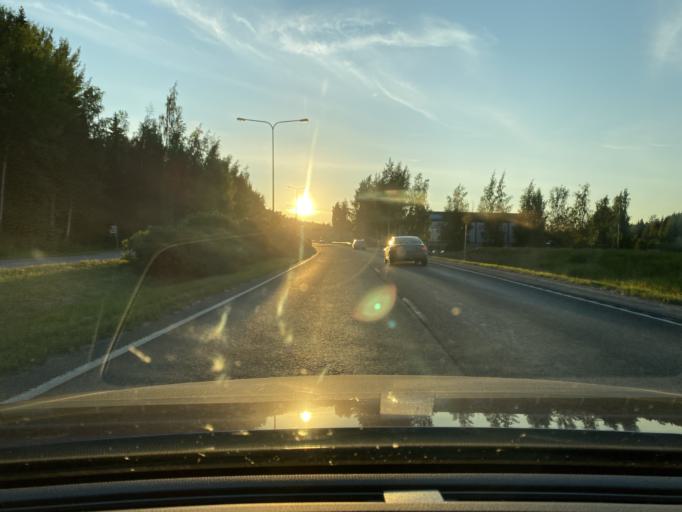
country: FI
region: Pirkanmaa
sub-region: Tampere
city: Yloejaervi
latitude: 61.5297
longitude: 23.6378
